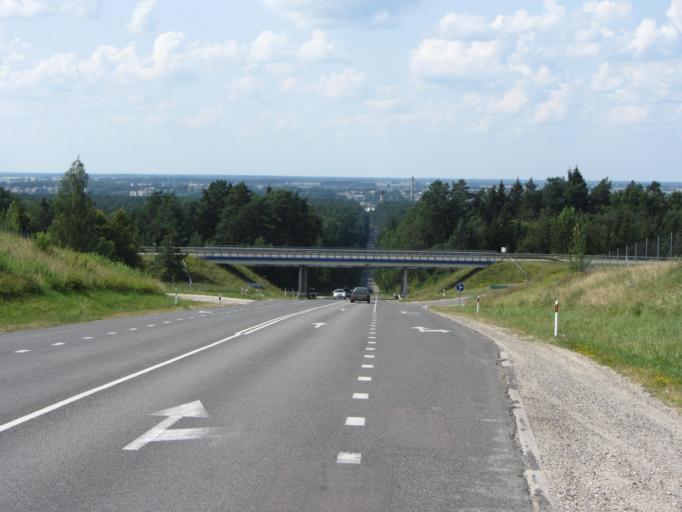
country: LT
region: Vilnius County
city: Ukmerge
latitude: 55.2275
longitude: 24.8226
